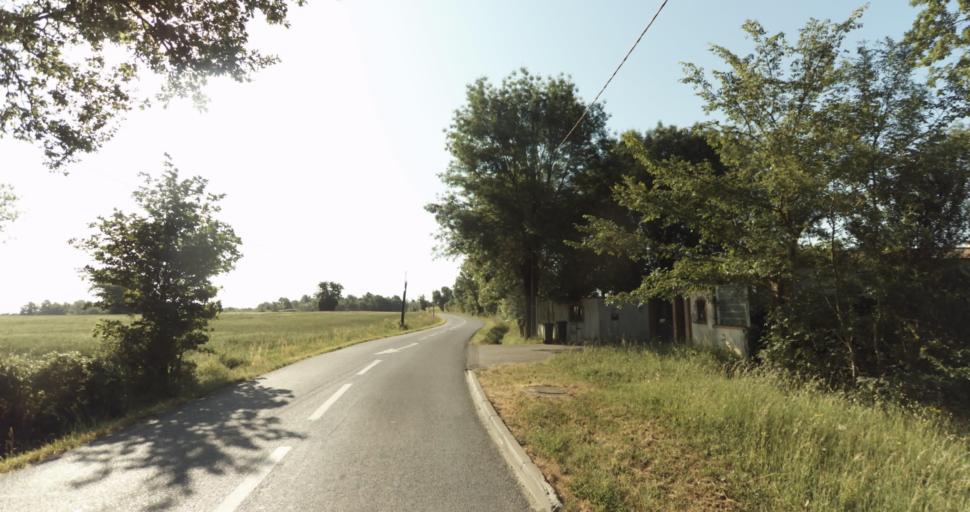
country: FR
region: Midi-Pyrenees
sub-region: Departement de la Haute-Garonne
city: Leguevin
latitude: 43.5797
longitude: 1.2202
